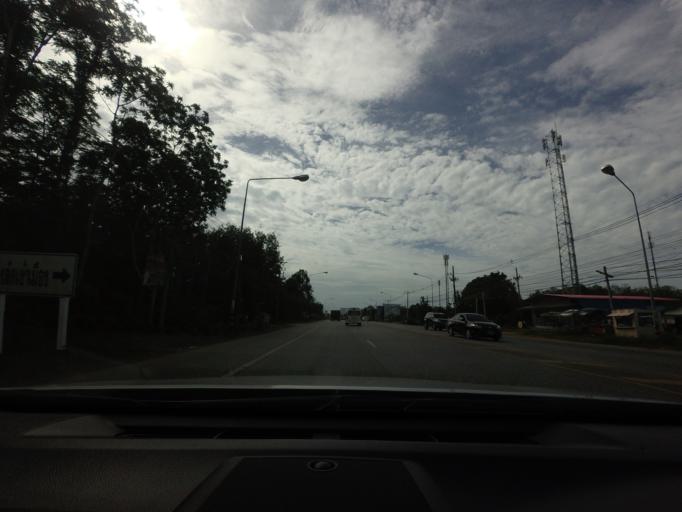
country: TH
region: Songkhla
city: Hat Yai
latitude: 6.9737
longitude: 100.4284
